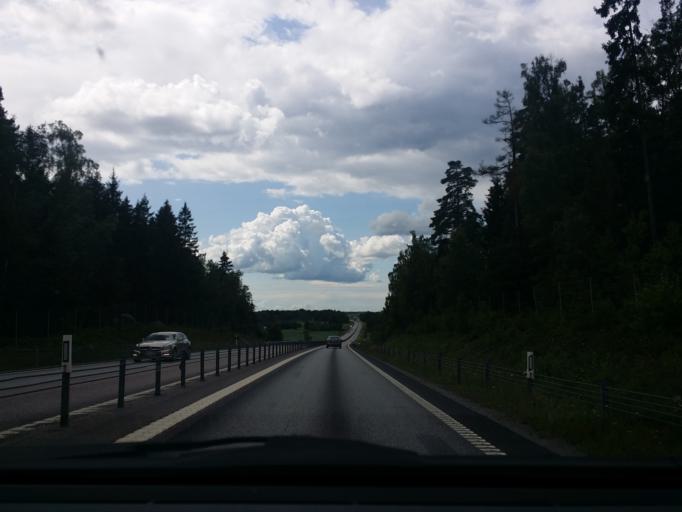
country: SE
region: Vaestmanland
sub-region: Kopings Kommun
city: Koping
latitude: 59.5404
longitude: 16.0026
